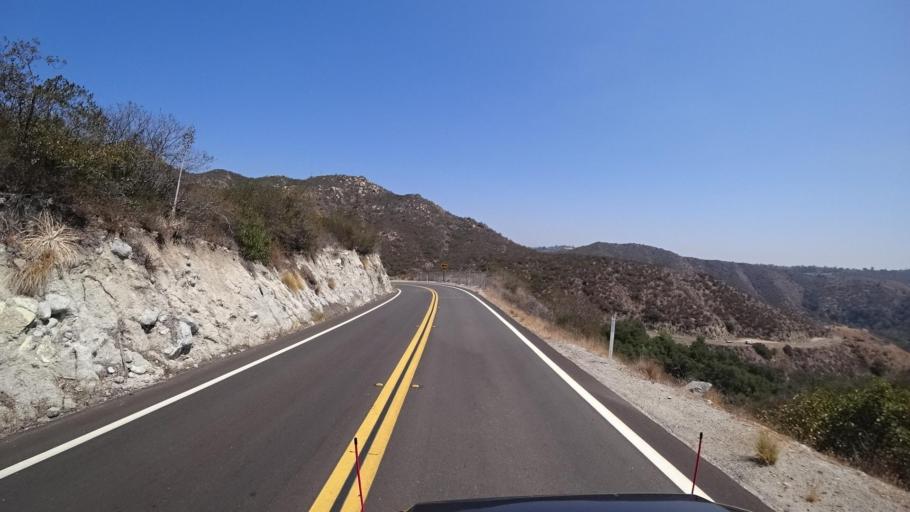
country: US
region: California
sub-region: San Diego County
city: Fallbrook
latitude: 33.4053
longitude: -117.2685
